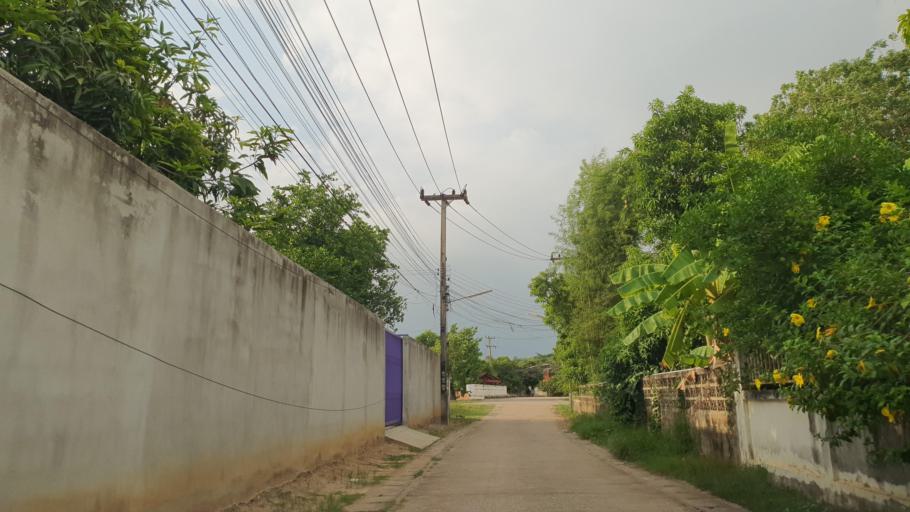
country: TH
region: Sukhothai
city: Ban Na
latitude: 17.0133
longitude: 99.7715
